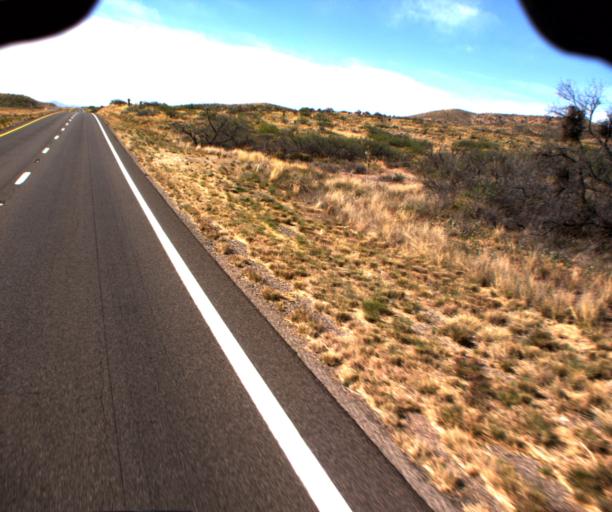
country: US
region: Arizona
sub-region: Graham County
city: Swift Trail Junction
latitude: 32.5186
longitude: -109.6741
